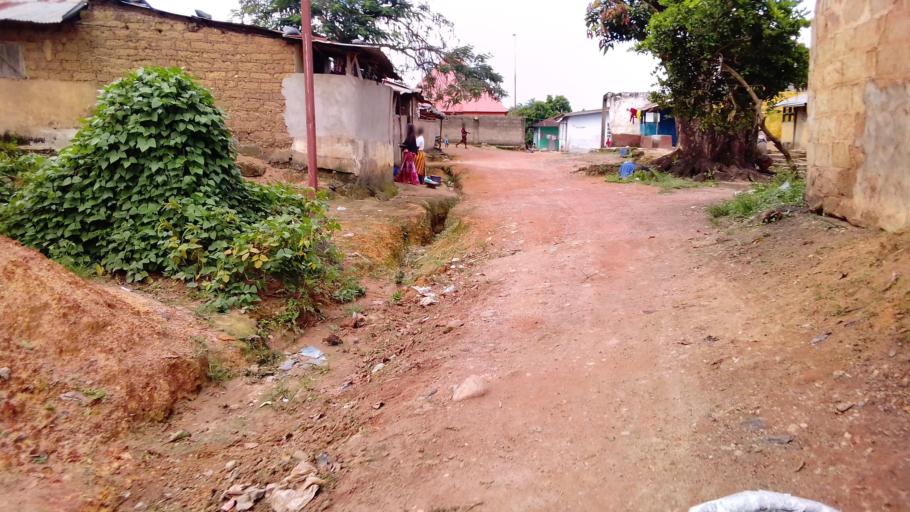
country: SL
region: Eastern Province
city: Koidu
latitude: 8.6507
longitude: -10.9730
